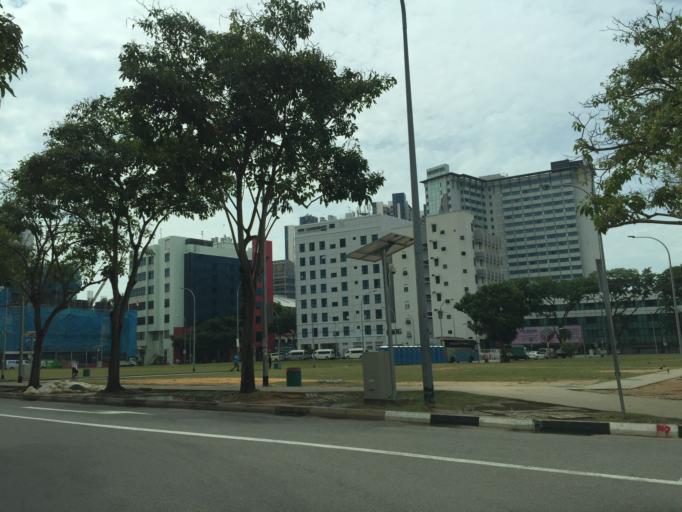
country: SG
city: Singapore
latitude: 1.3117
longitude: 103.8535
